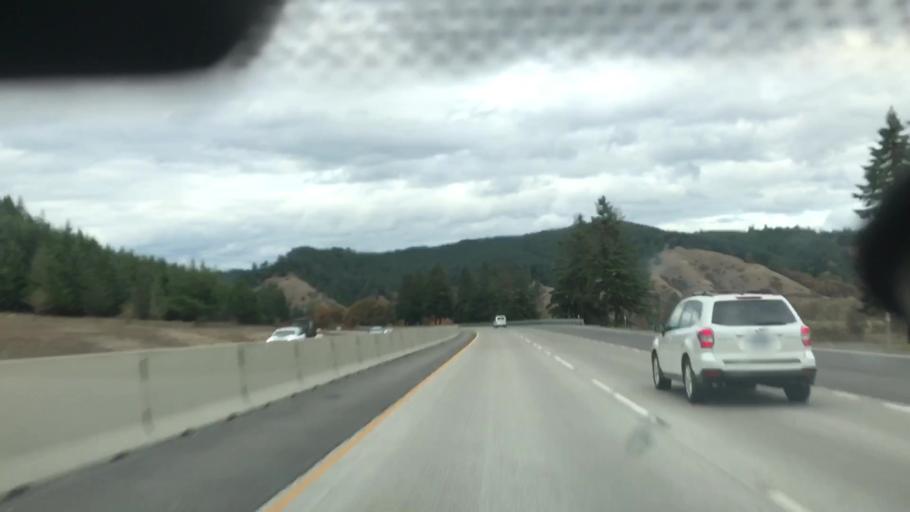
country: US
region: Oregon
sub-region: Douglas County
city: Yoncalla
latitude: 43.6125
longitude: -123.2171
